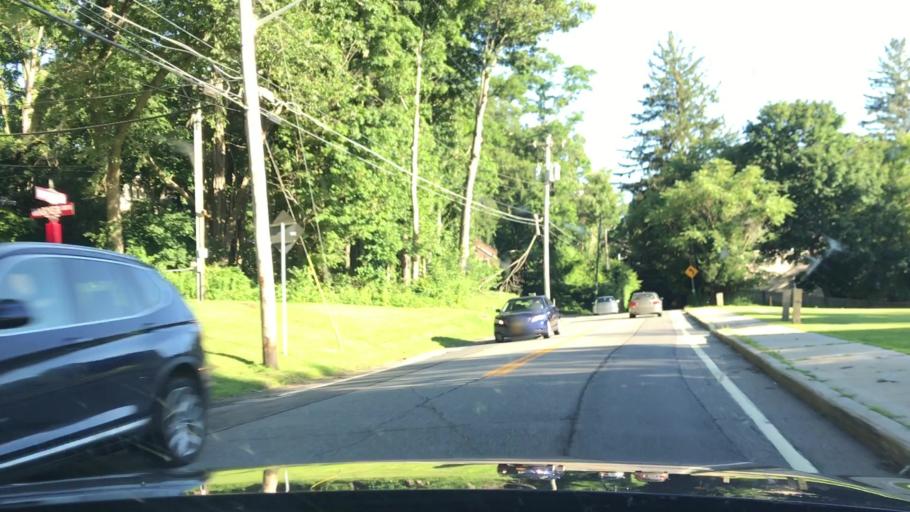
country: US
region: New York
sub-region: Westchester County
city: Heritage Hills
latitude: 41.3485
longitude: -73.6613
